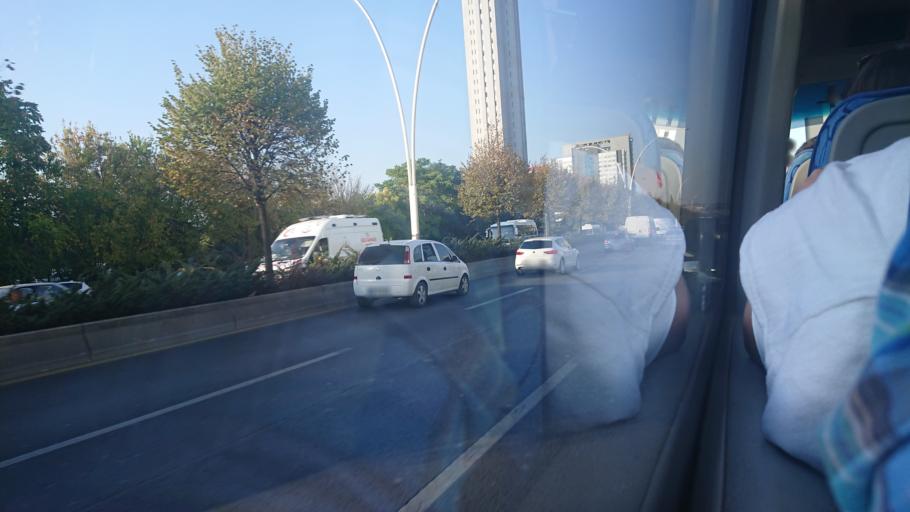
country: TR
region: Ankara
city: Ankara
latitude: 39.9358
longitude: 32.8230
